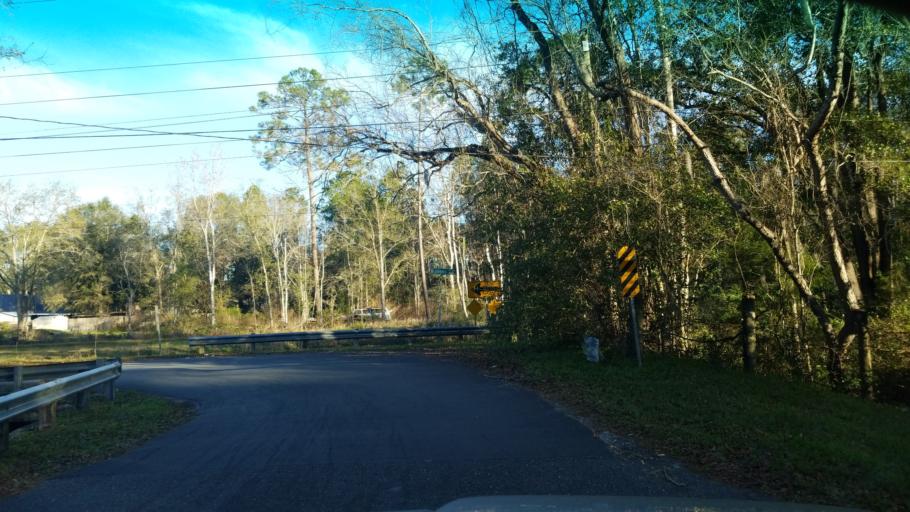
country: US
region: Florida
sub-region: Duval County
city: Baldwin
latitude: 30.3234
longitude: -81.8444
